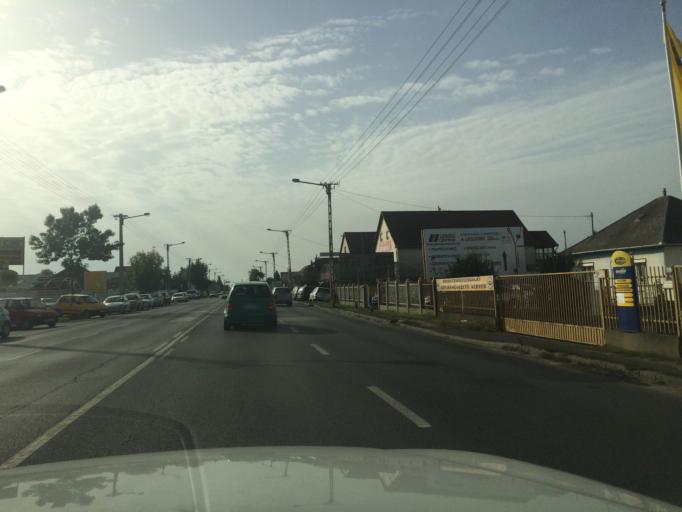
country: HU
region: Szabolcs-Szatmar-Bereg
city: Nyiregyhaza
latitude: 47.9291
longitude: 21.7187
